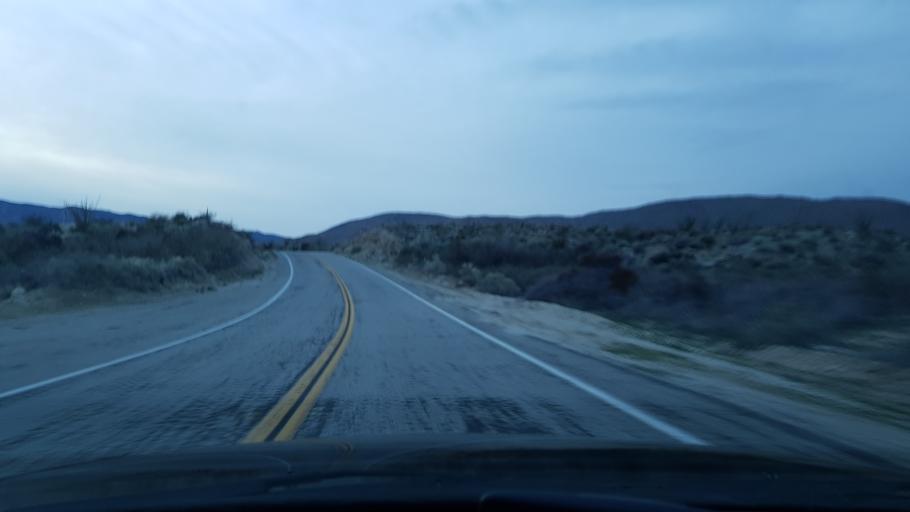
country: US
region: California
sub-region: San Diego County
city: Pine Valley
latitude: 32.9758
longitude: -116.3471
